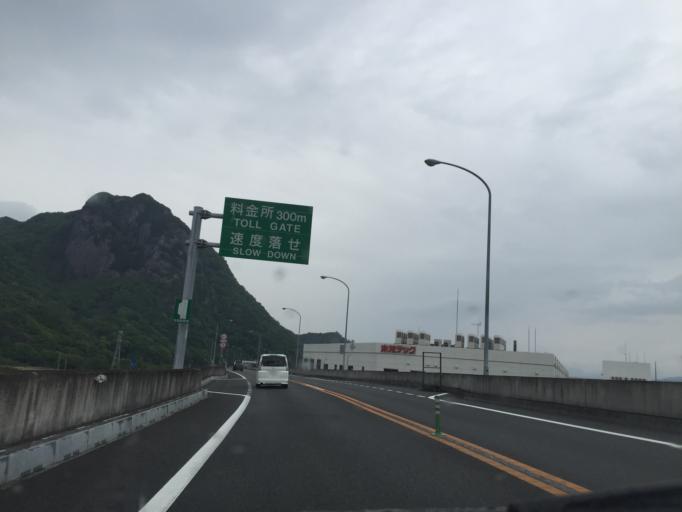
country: JP
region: Shizuoka
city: Mishima
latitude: 34.9947
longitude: 138.9359
